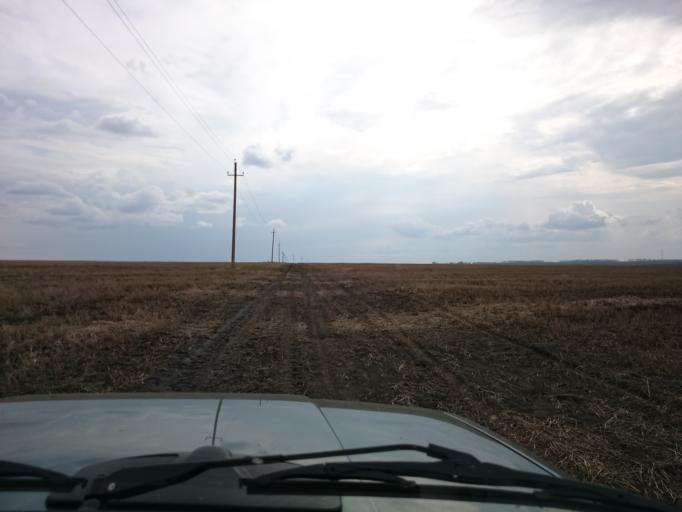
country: RU
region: Mordoviya
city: Kadoshkino
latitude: 54.0258
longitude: 44.4773
